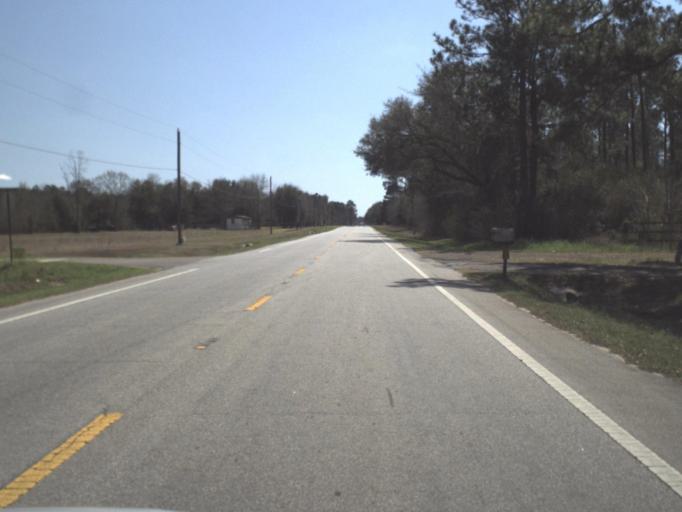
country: US
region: Florida
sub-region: Gadsden County
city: Gretna
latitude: 30.6938
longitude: -84.6232
